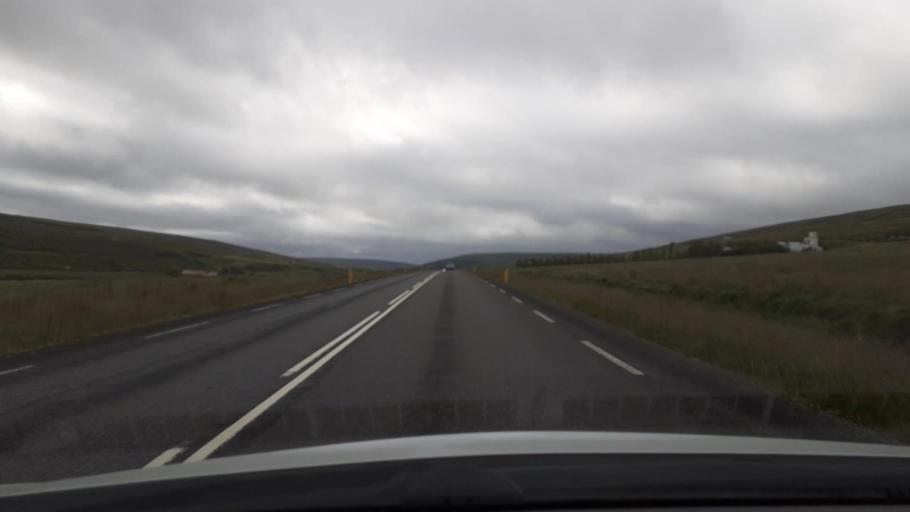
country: IS
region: Northeast
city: Laugar
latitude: 65.7100
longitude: -17.3634
